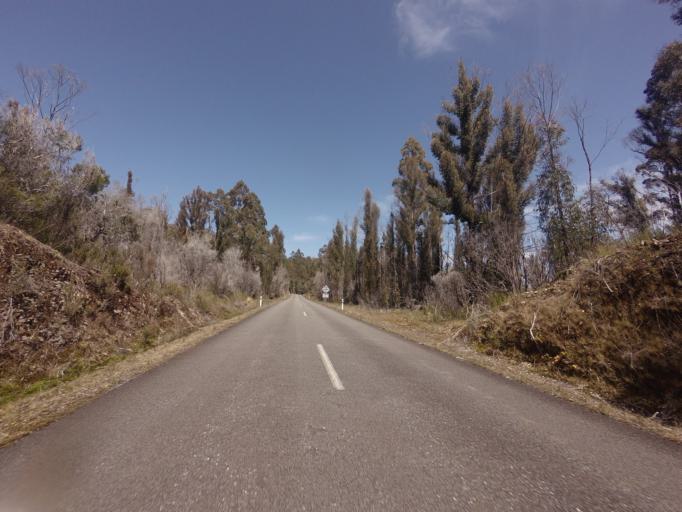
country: AU
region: Tasmania
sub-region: Huon Valley
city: Geeveston
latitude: -42.8340
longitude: 146.2675
